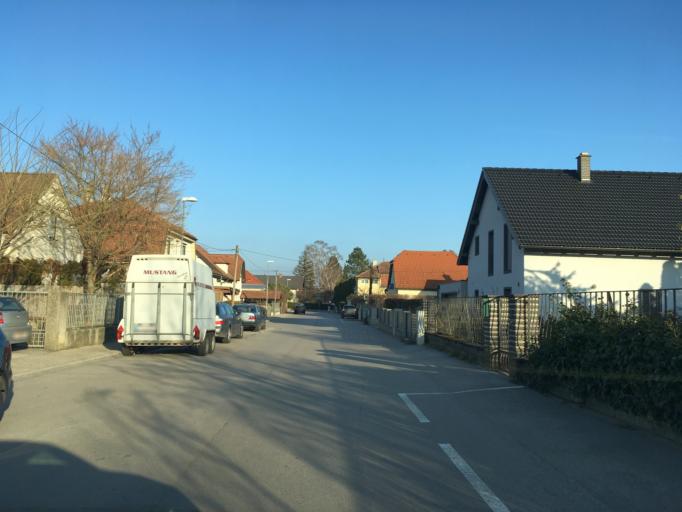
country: AT
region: Lower Austria
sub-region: Politischer Bezirk Tulln
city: Tulbing
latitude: 48.3300
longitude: 16.1196
